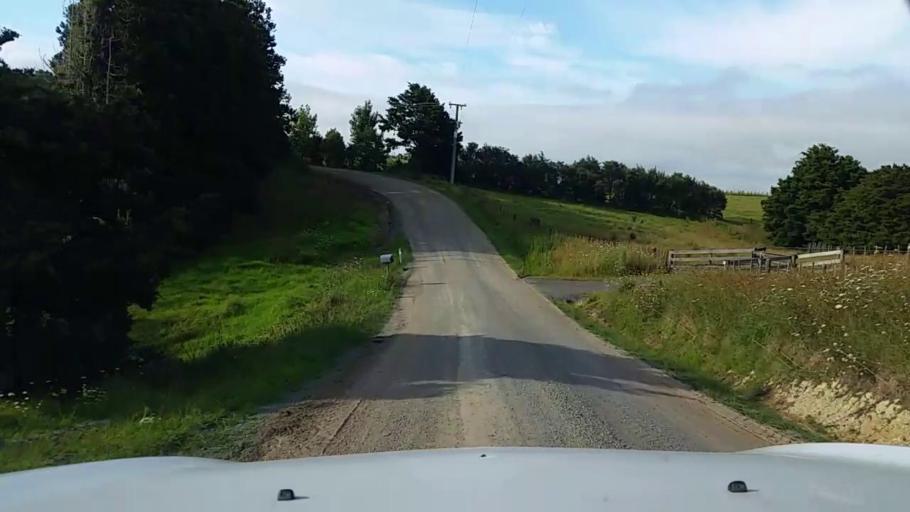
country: NZ
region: Northland
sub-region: Whangarei
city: Maungatapere
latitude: -35.6742
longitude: 174.1765
